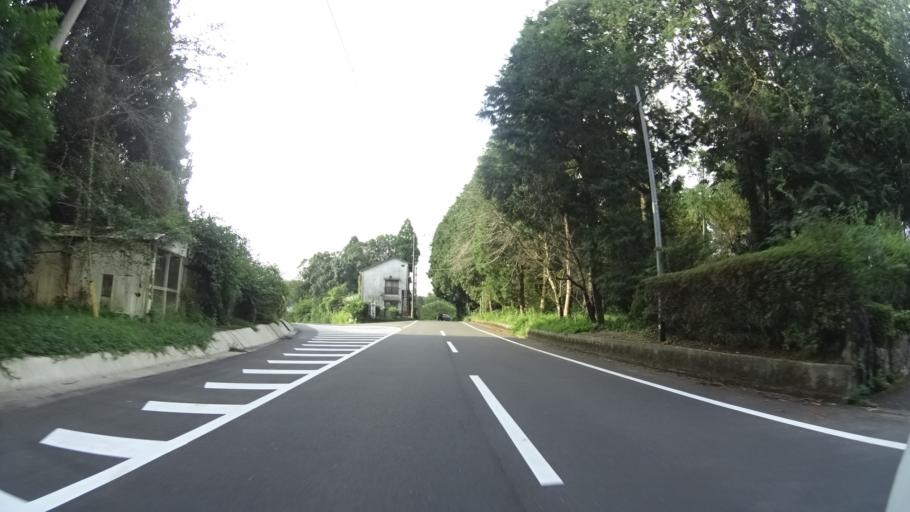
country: JP
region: Kagoshima
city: Okuchi-shinohara
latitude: 32.0144
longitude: 130.5772
